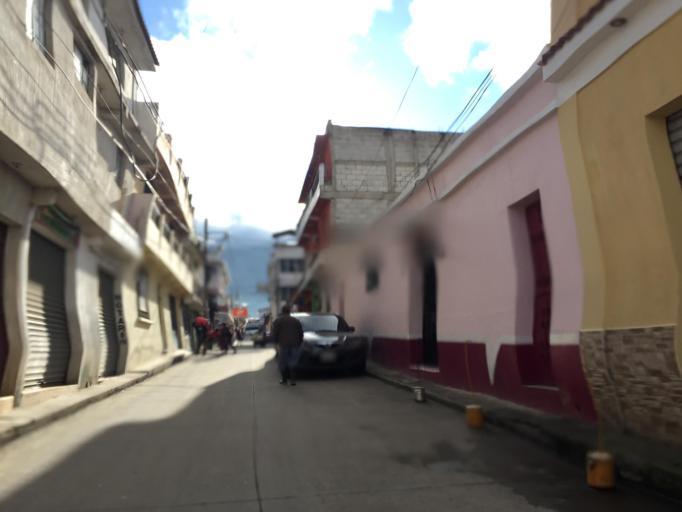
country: GT
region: Totonicapan
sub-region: Municipio de Totonicapan
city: Totonicapan
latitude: 14.9106
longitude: -91.3633
